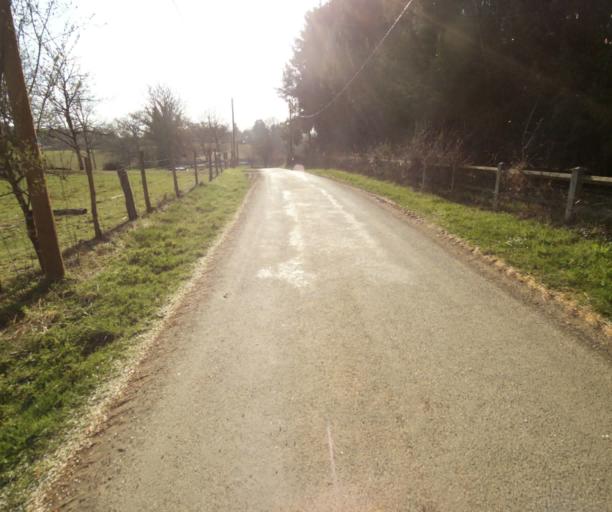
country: FR
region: Limousin
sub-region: Departement de la Correze
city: Saint-Mexant
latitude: 45.3422
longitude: 1.6174
